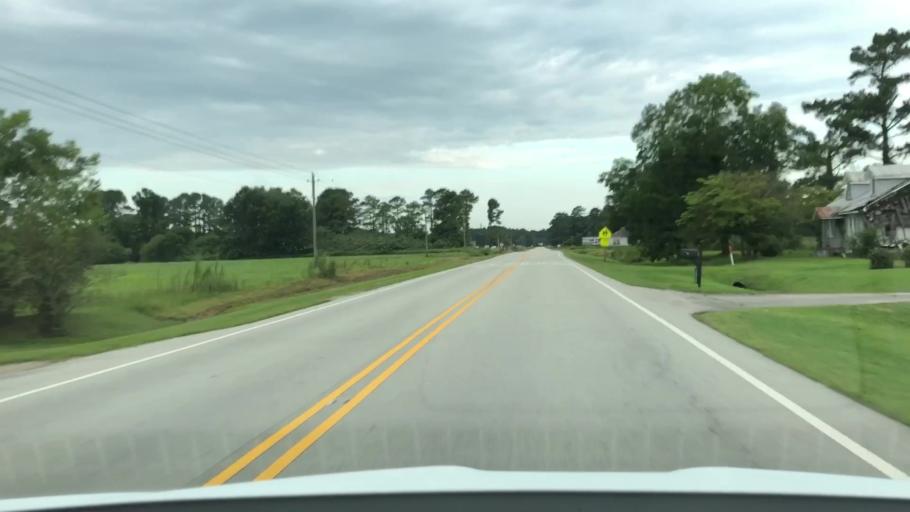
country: US
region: North Carolina
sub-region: Jones County
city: Trenton
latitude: 35.0343
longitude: -77.3286
